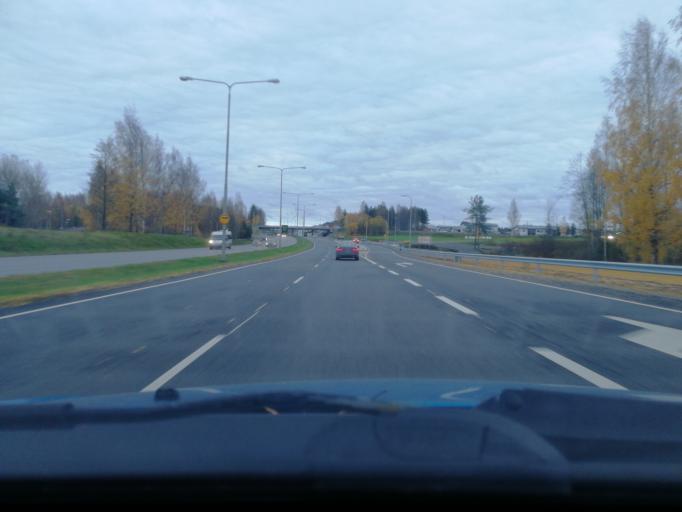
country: FI
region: Pirkanmaa
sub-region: Tampere
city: Tampere
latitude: 61.4823
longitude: 23.8285
